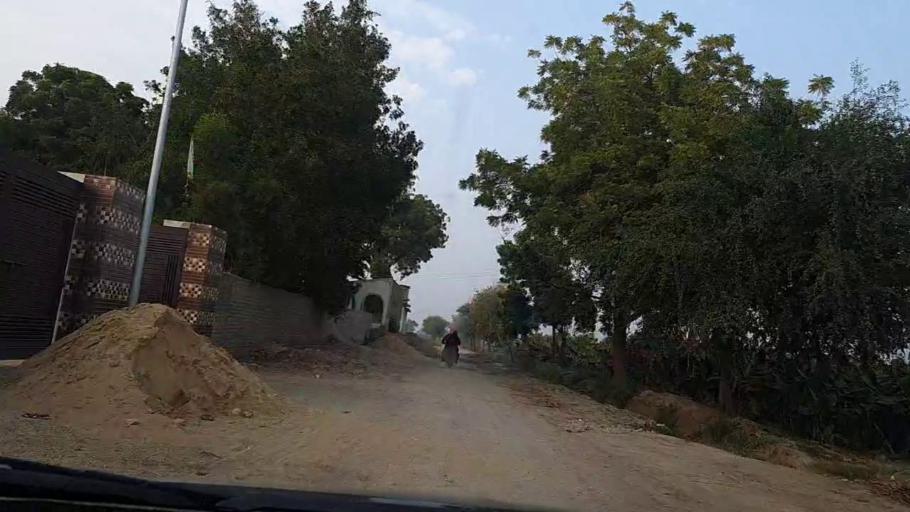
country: PK
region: Sindh
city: Nawabshah
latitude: 26.2849
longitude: 68.3211
